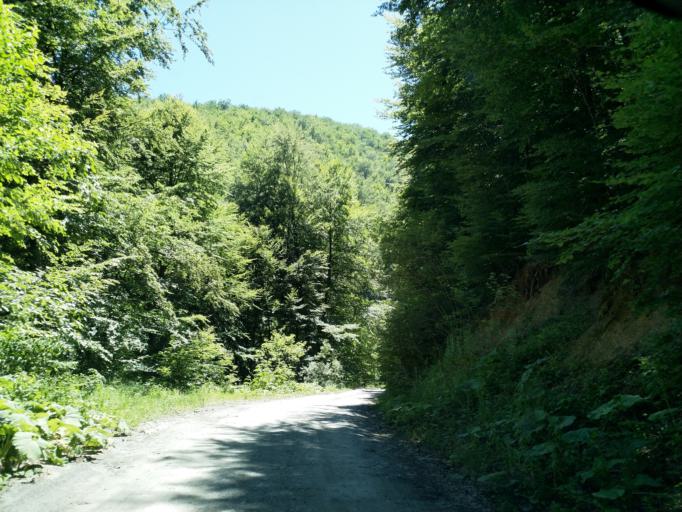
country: XK
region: Mitrovica
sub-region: Komuna e Leposaviqit
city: Leposaviq
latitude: 43.2768
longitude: 20.8686
